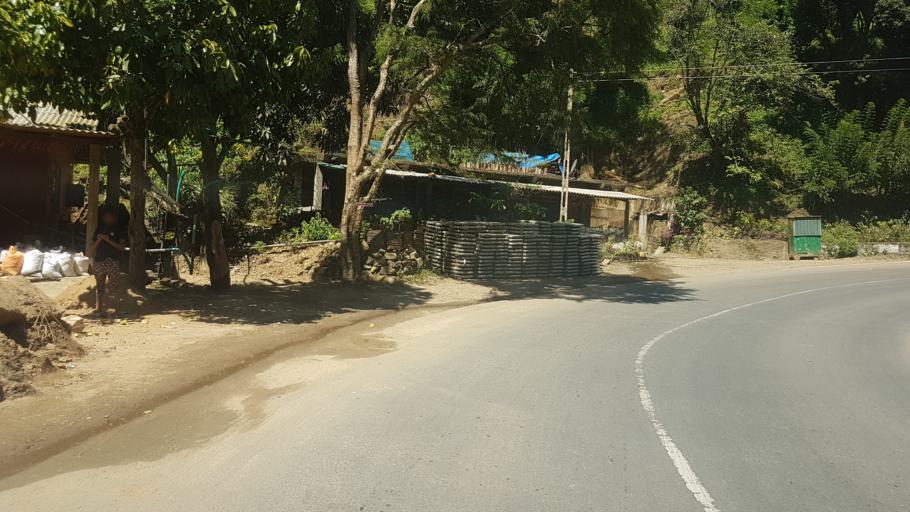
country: LK
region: Uva
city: Badulla
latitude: 6.8678
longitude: 81.0461
